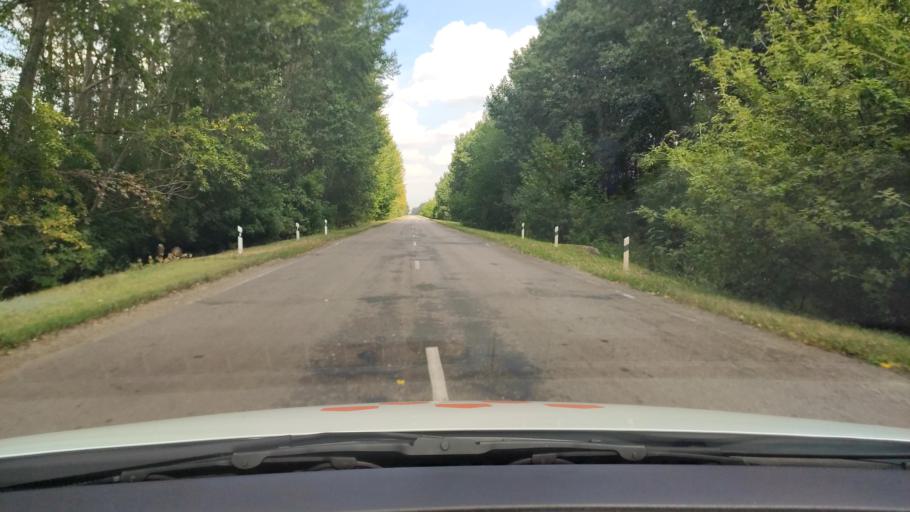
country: RU
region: Voronezj
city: Pereleshinskiy
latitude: 51.7179
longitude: 40.3476
